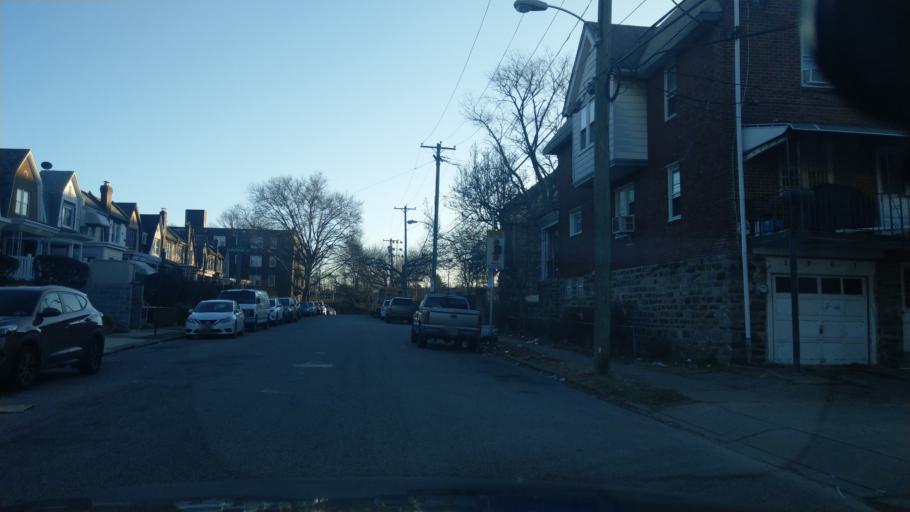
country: US
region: Pennsylvania
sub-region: Montgomery County
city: Wyncote
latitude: 40.0525
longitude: -75.1467
